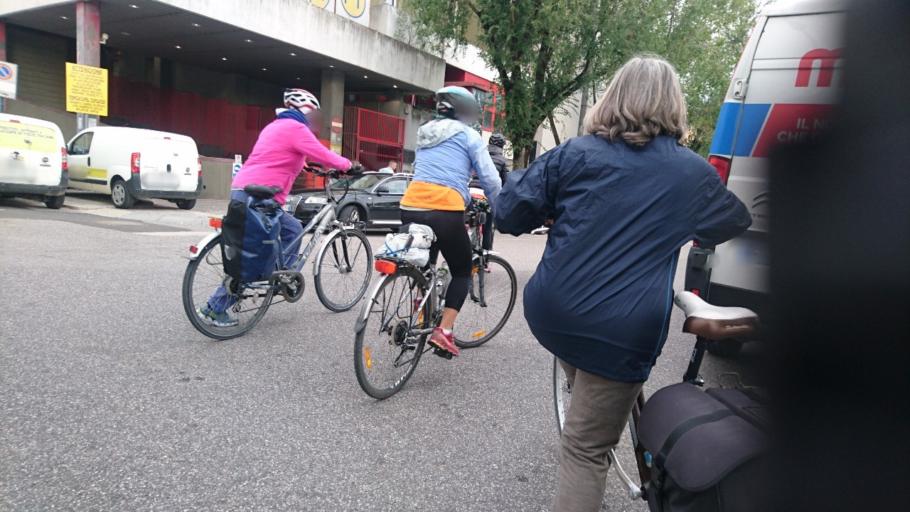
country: IT
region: Veneto
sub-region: Provincia di Verona
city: Verona
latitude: 45.4296
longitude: 10.9809
